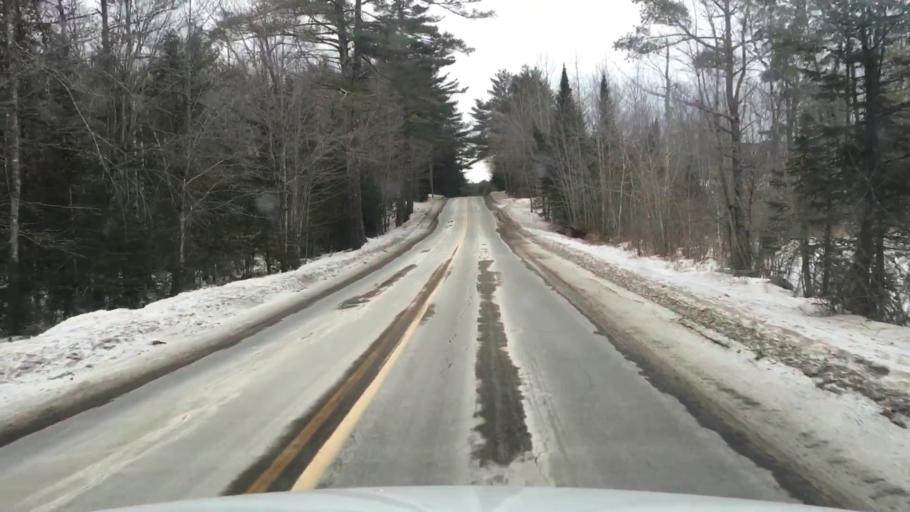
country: US
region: Maine
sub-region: Lincoln County
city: Whitefield
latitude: 44.2387
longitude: -69.6231
